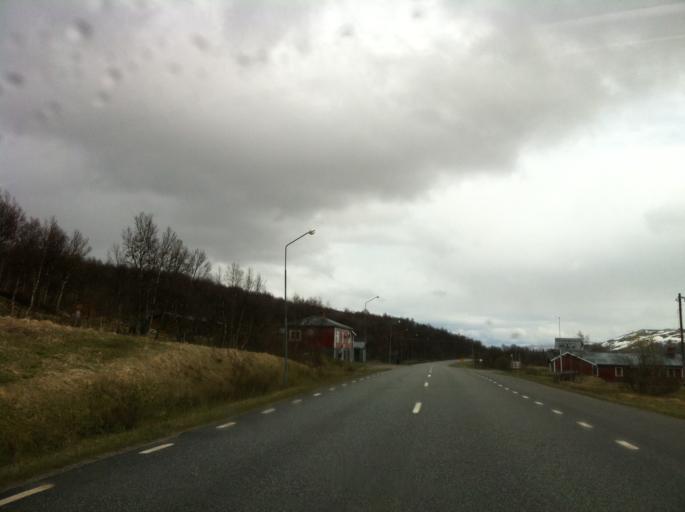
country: NO
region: Sor-Trondelag
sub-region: Tydal
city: Aas
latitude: 62.5933
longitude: 12.1863
